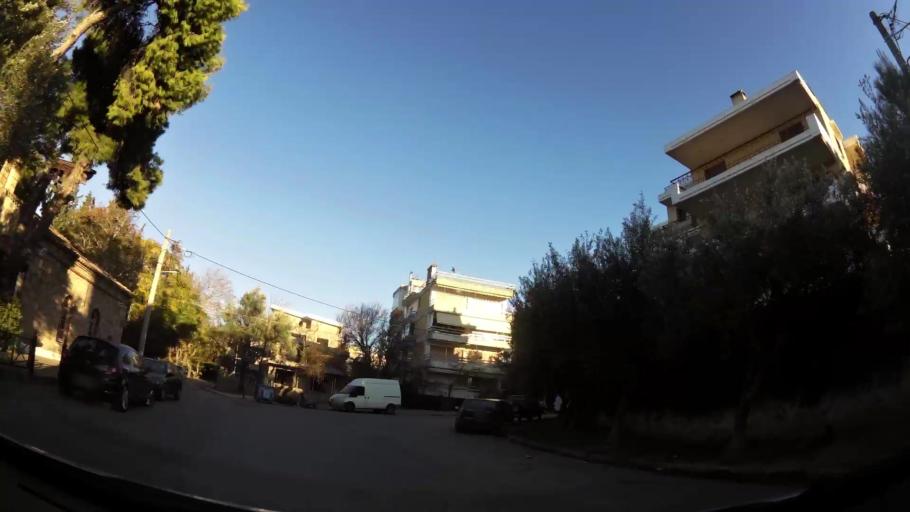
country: GR
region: Attica
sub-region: Nomarchia Athinas
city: Kifisia
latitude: 38.0699
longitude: 23.8018
